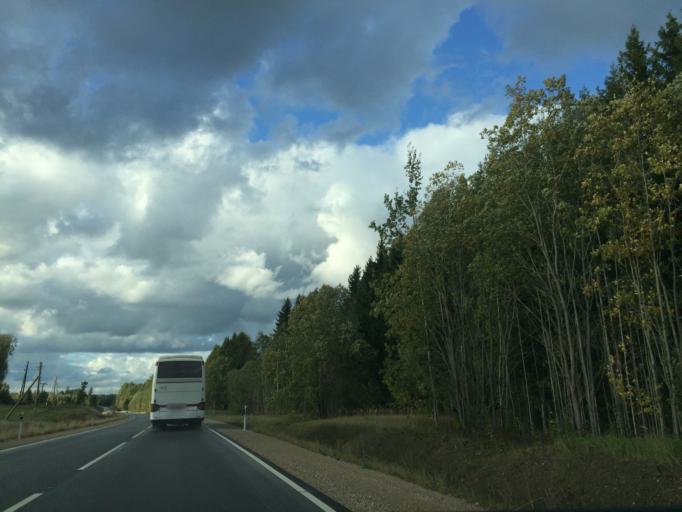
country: LV
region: Ligatne
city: Ligatne
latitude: 57.1429
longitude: 25.0793
